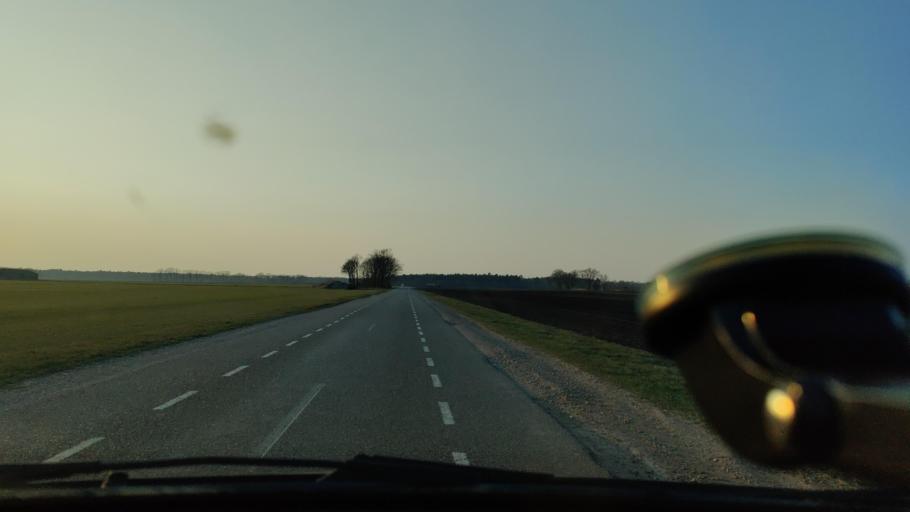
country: NL
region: Limburg
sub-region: Gemeente Bergen
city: Wellerlooi
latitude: 51.5706
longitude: 6.1407
